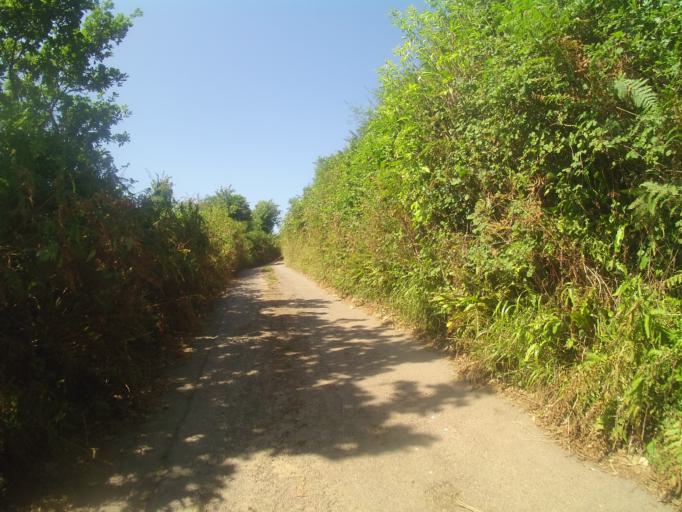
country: GB
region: England
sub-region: Devon
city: Dartmouth
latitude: 50.3632
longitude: -3.6223
